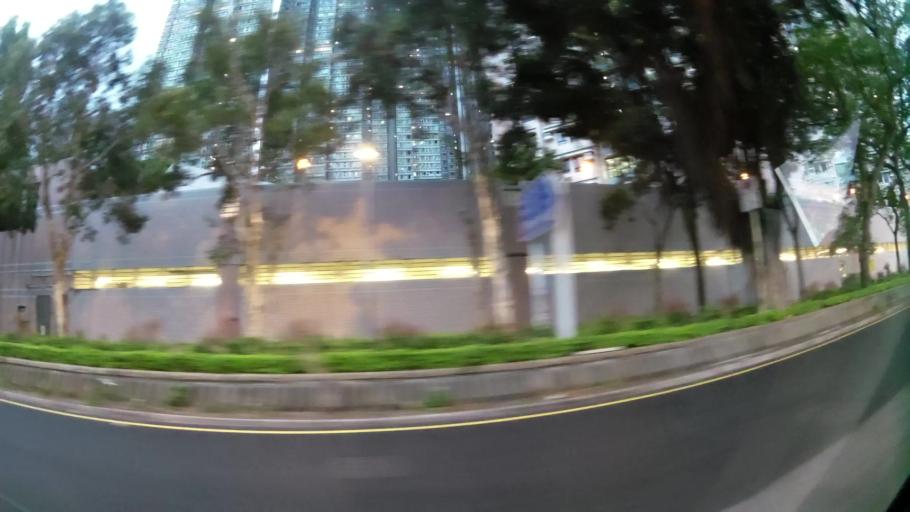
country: HK
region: Sham Shui Po
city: Sham Shui Po
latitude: 22.3237
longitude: 114.1591
